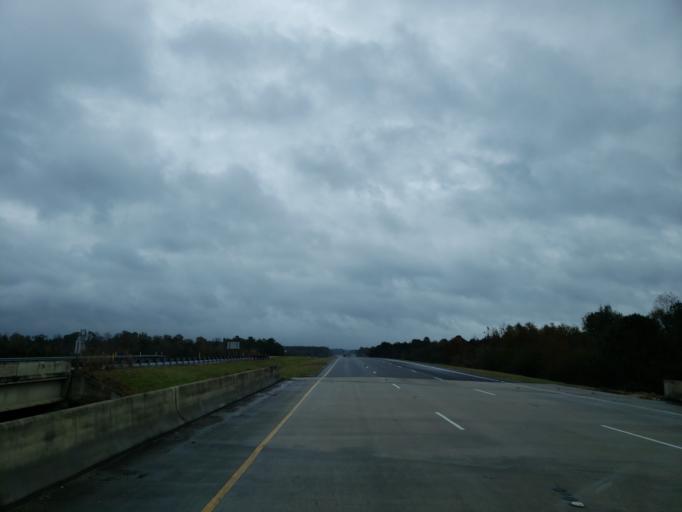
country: US
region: Mississippi
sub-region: Clarke County
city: Quitman
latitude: 31.9788
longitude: -88.7205
